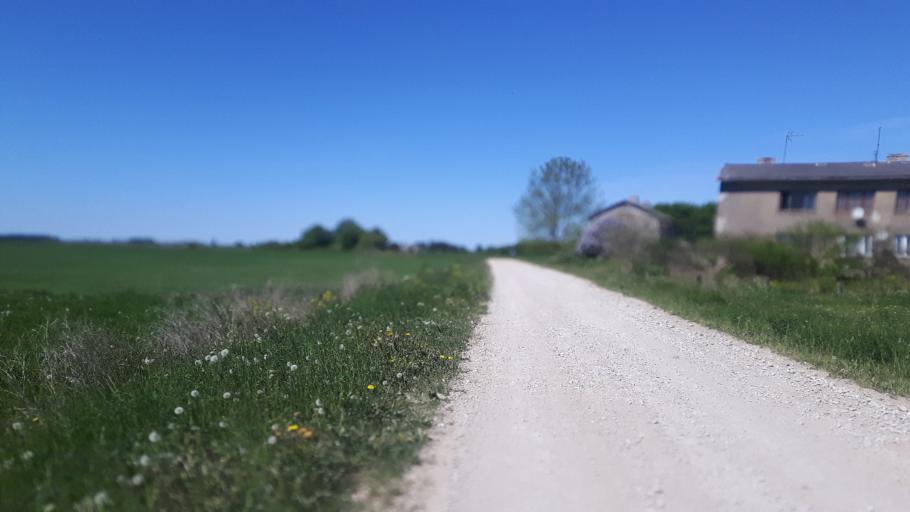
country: EE
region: Ida-Virumaa
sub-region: Toila vald
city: Voka
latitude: 59.4025
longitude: 27.6652
